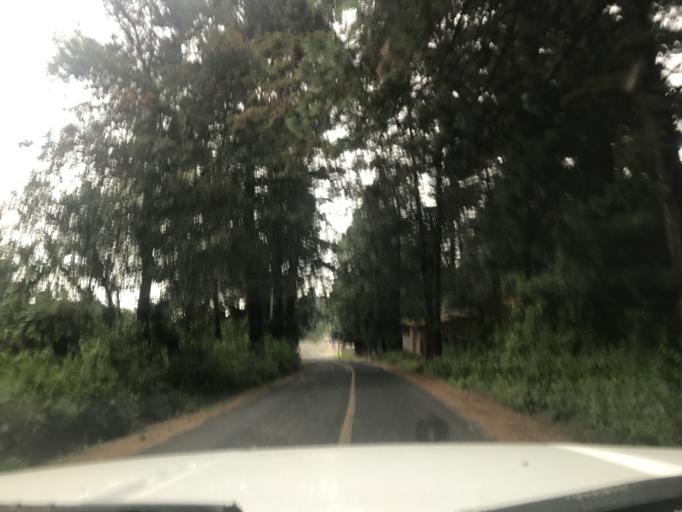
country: MX
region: Morelos
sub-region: Ocuituco
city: Huepalcalco (San Miguel)
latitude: 18.9134
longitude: -98.7523
